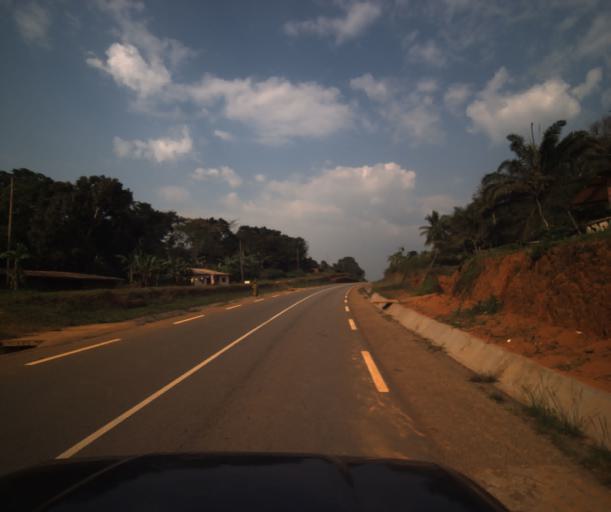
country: CM
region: Centre
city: Mbankomo
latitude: 3.6518
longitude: 11.3338
